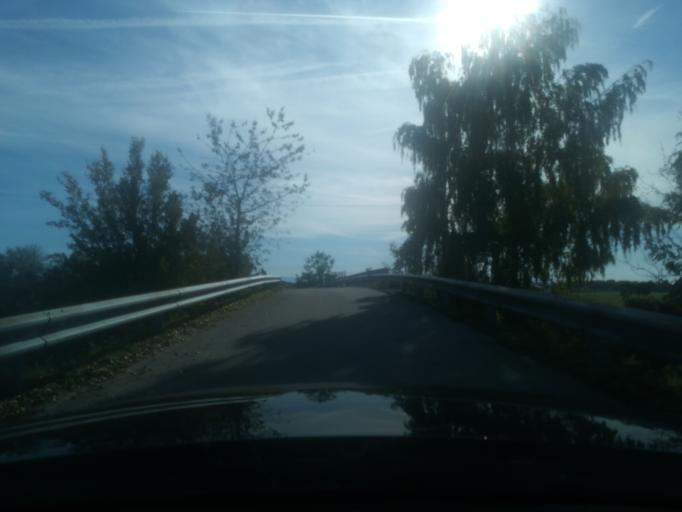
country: AT
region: Upper Austria
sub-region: Wels-Land
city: Marchtrenk
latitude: 48.2068
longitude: 14.1458
